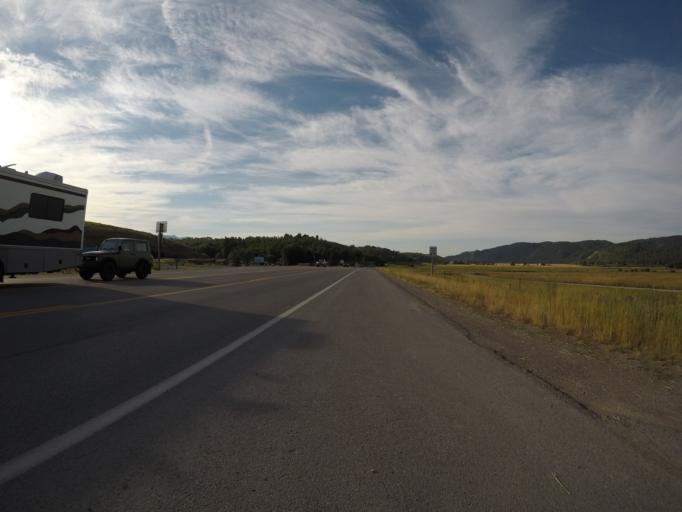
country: US
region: Wyoming
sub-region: Lincoln County
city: Afton
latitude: 42.9126
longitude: -110.9997
